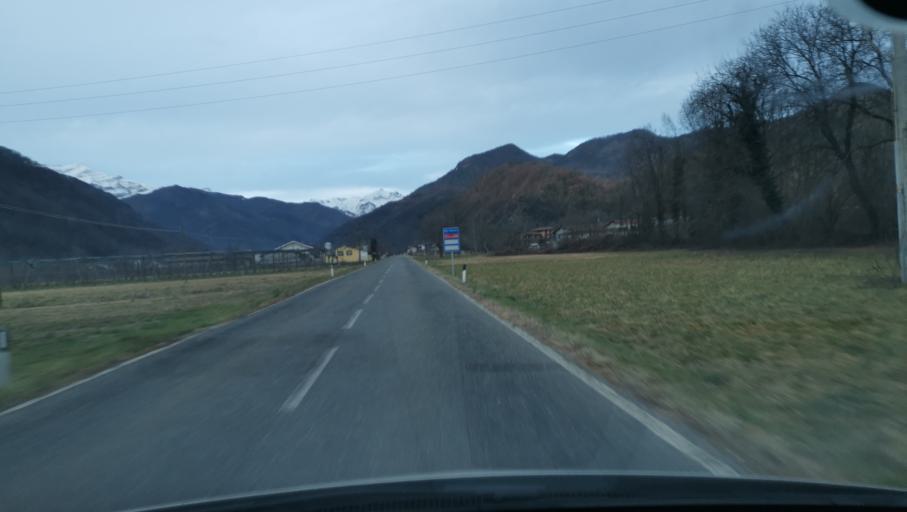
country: IT
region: Piedmont
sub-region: Provincia di Cuneo
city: Valgrana
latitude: 44.4124
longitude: 7.3625
